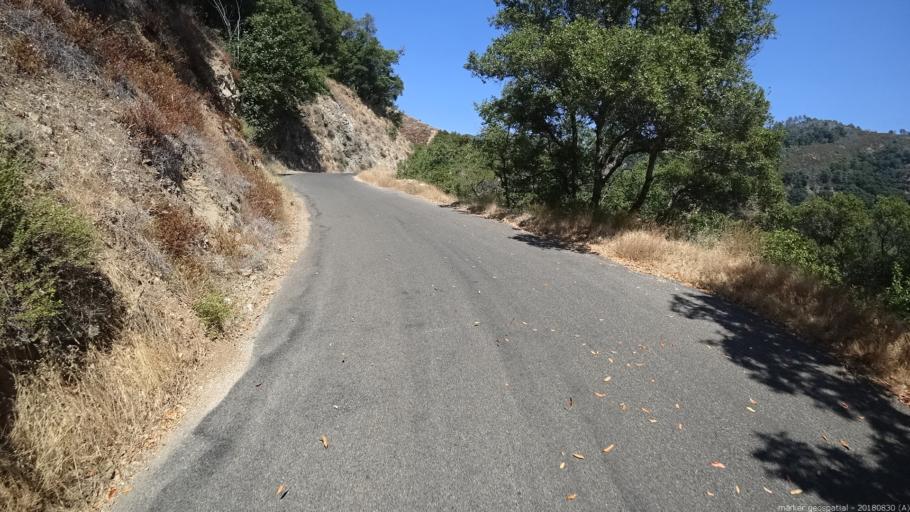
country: US
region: California
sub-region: Monterey County
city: Greenfield
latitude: 36.0008
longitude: -121.4582
